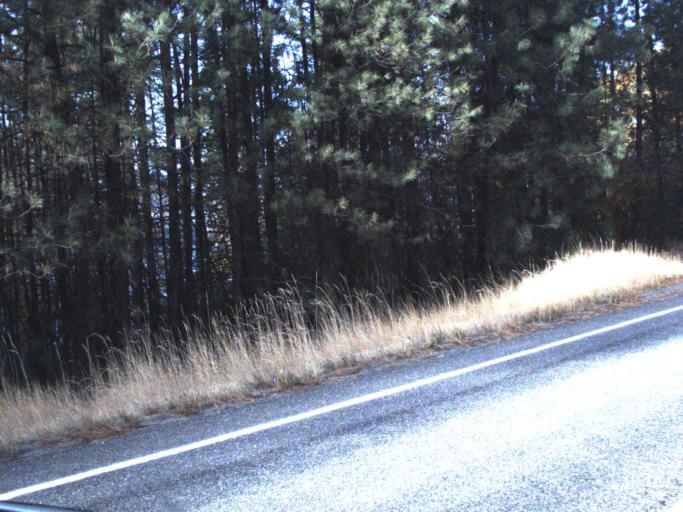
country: US
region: Washington
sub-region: Stevens County
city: Kettle Falls
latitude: 48.5244
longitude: -118.1377
